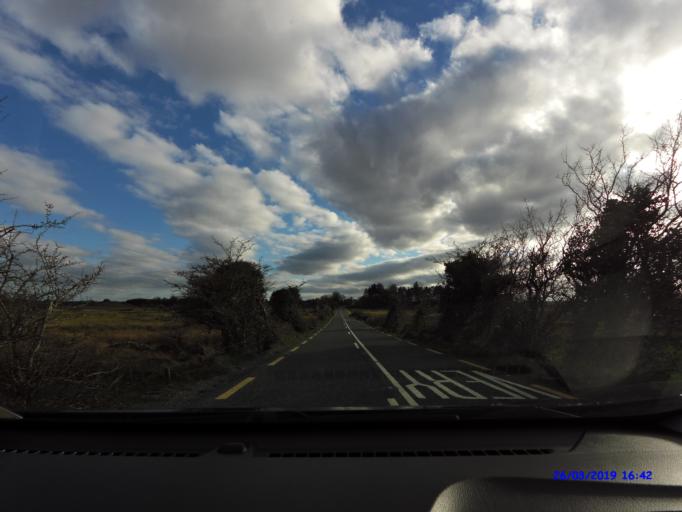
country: IE
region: Connaught
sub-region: Maigh Eo
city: Ballyhaunis
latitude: 53.8645
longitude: -8.7634
